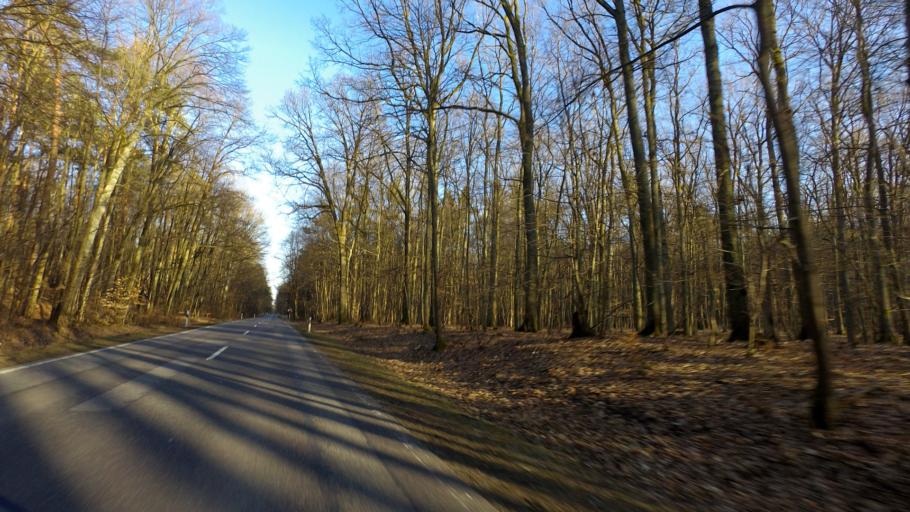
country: DE
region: Brandenburg
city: Joachimsthal
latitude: 52.9532
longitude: 13.7675
